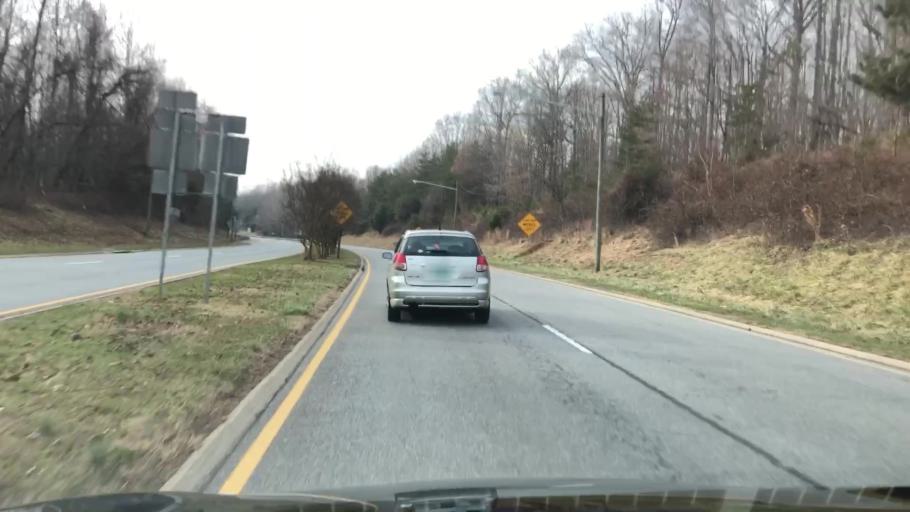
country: US
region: Virginia
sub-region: City of Lynchburg
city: West Lynchburg
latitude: 37.4408
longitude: -79.2337
